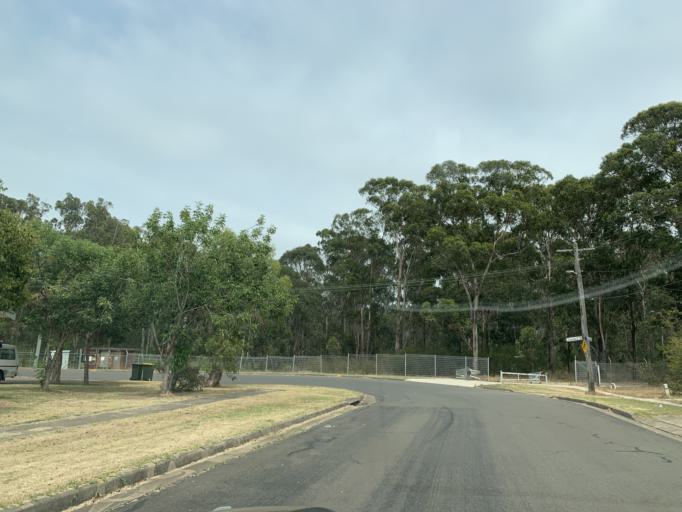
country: AU
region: New South Wales
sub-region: Blacktown
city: Doonside
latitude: -33.7624
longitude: 150.8860
